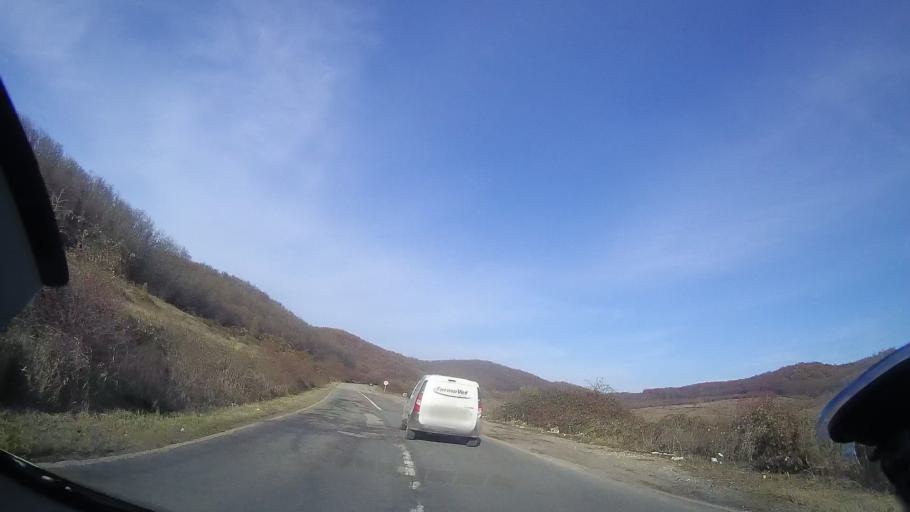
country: RO
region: Bihor
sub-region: Comuna Tileagd
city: Tileagd
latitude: 47.0890
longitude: 22.2352
